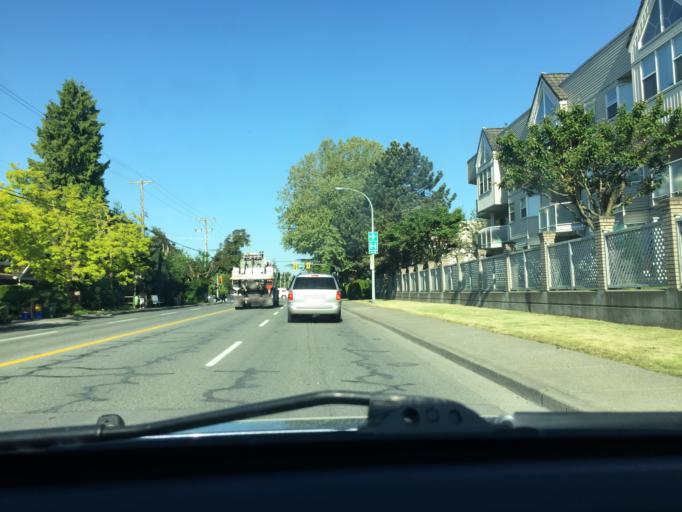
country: CA
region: British Columbia
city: Richmond
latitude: 49.1556
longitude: -123.1463
